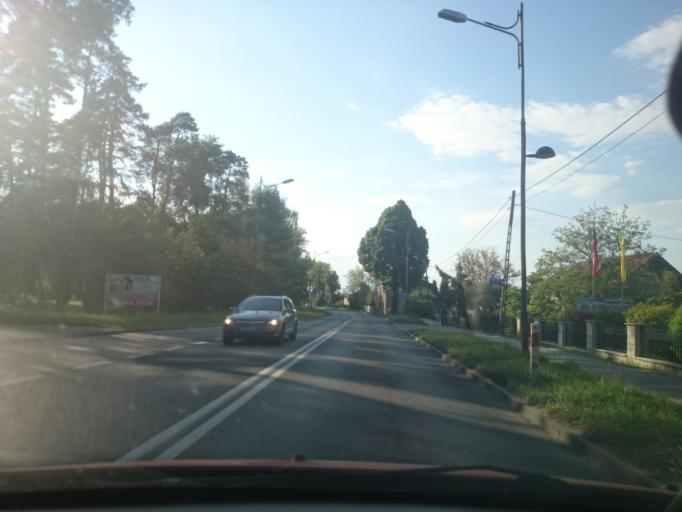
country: PL
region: Opole Voivodeship
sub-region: Powiat strzelecki
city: Strzelce Opolskie
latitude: 50.5180
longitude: 18.2868
